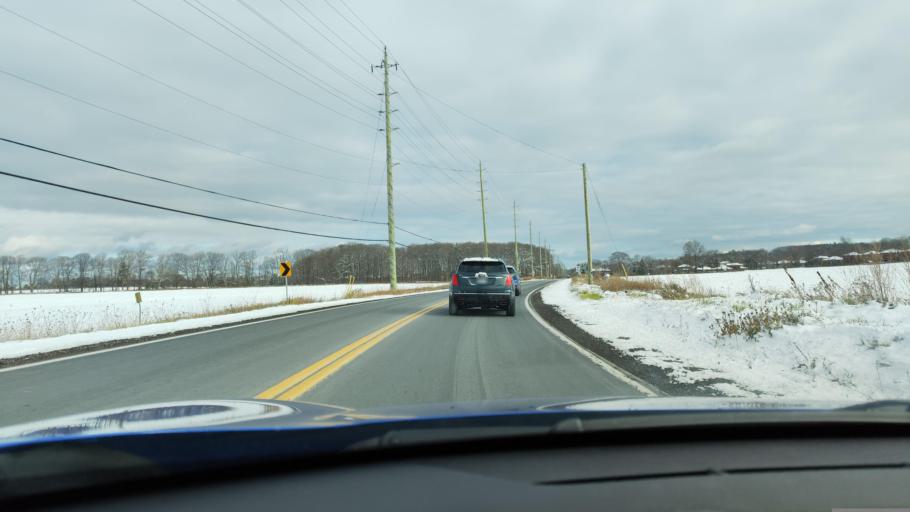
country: CA
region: Ontario
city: Barrie
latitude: 44.4011
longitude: -79.7375
